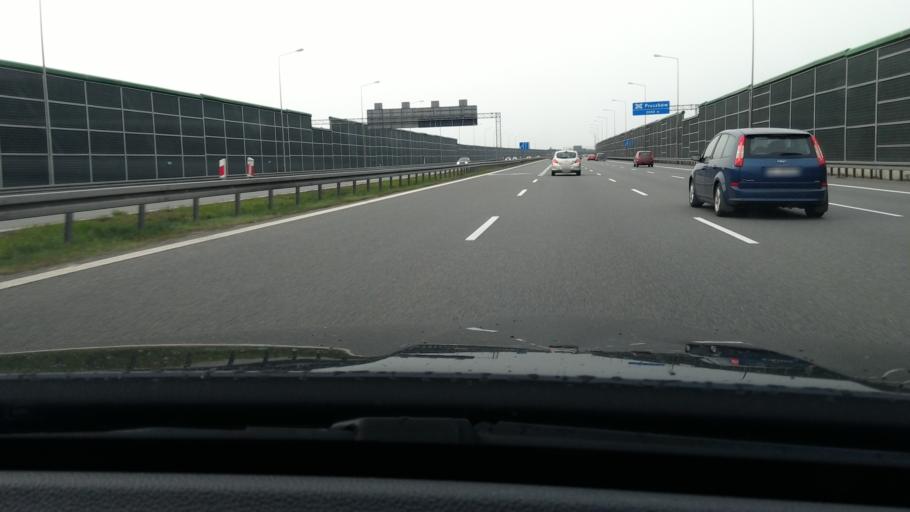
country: PL
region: Masovian Voivodeship
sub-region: Powiat pruszkowski
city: Piastow
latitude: 52.1964
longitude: 20.8276
